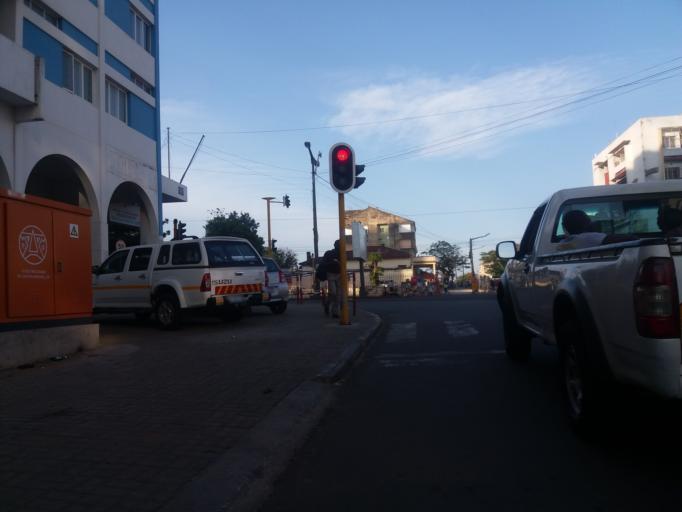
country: MZ
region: Maputo City
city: Maputo
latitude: -25.9611
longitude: 32.5700
